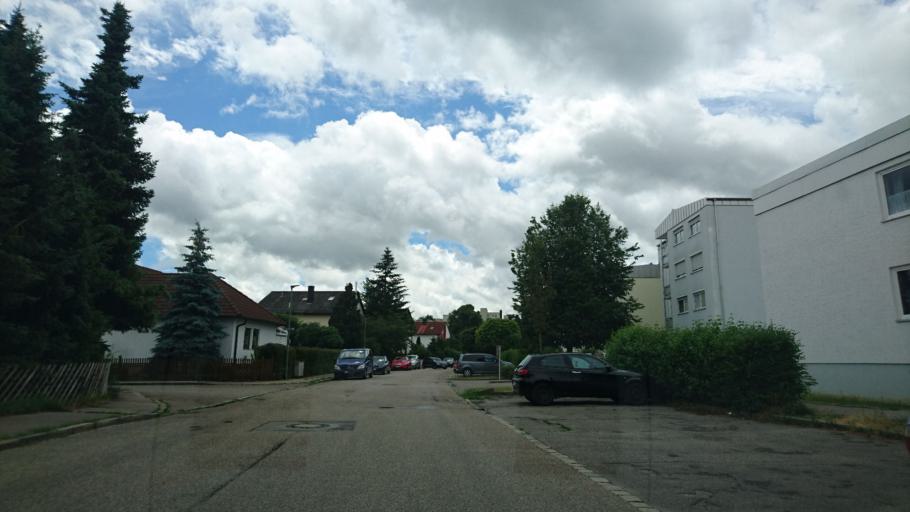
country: DE
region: Bavaria
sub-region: Lower Bavaria
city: Landshut
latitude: 48.5515
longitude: 12.1183
